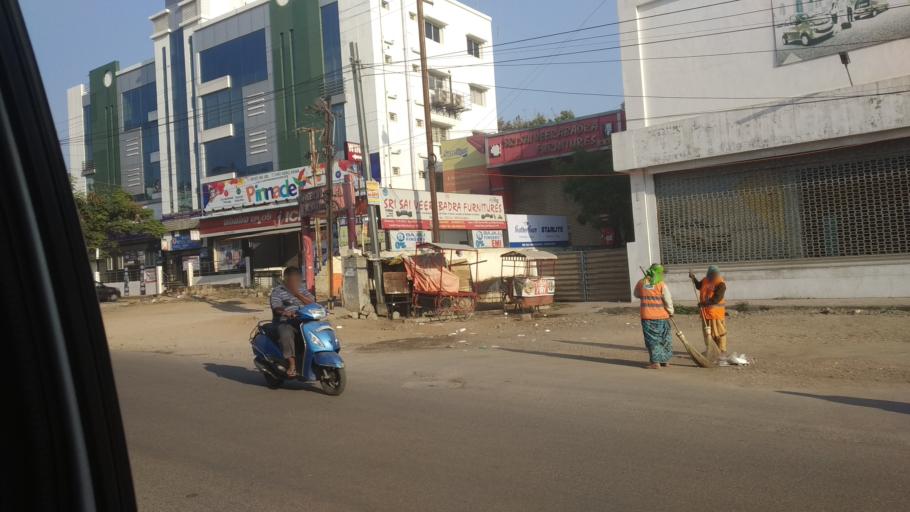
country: IN
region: Telangana
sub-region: Rangareddi
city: Kukatpalli
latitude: 17.4559
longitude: 78.4468
